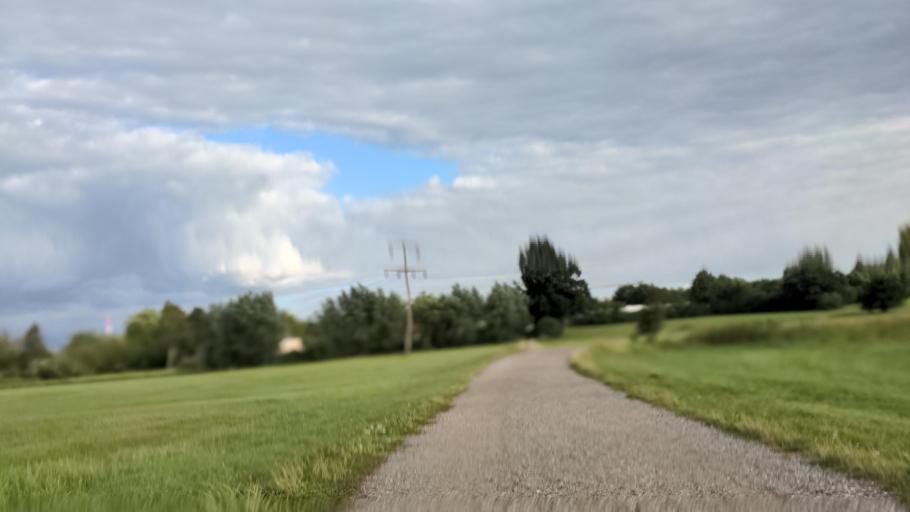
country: DE
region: Schleswig-Holstein
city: Neustadt in Holstein
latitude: 54.1030
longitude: 10.7944
